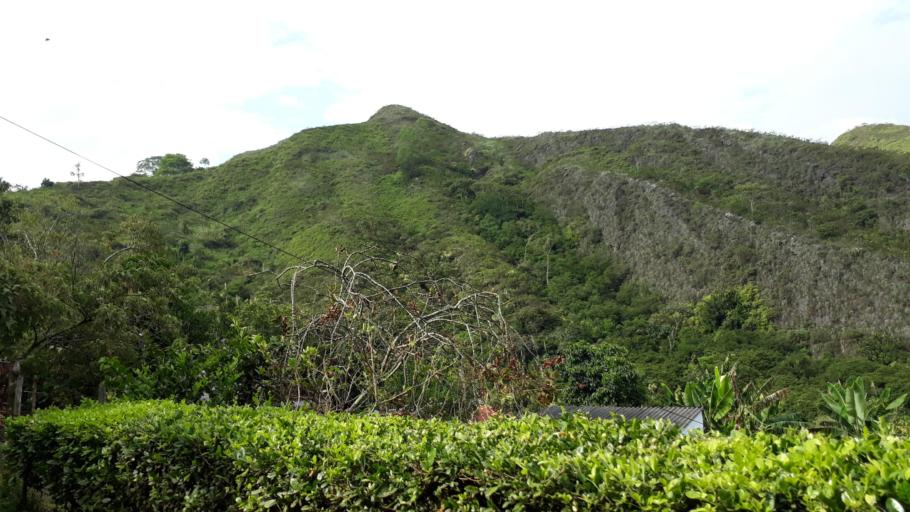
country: CO
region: Valle del Cauca
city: Jamundi
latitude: 3.2214
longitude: -76.6259
